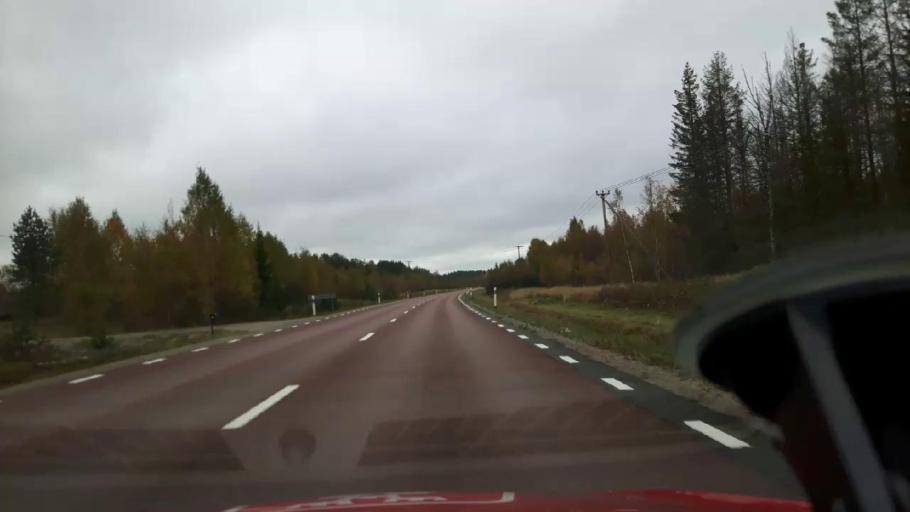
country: SE
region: Jaemtland
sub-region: Harjedalens Kommun
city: Sveg
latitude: 62.2575
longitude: 14.8188
